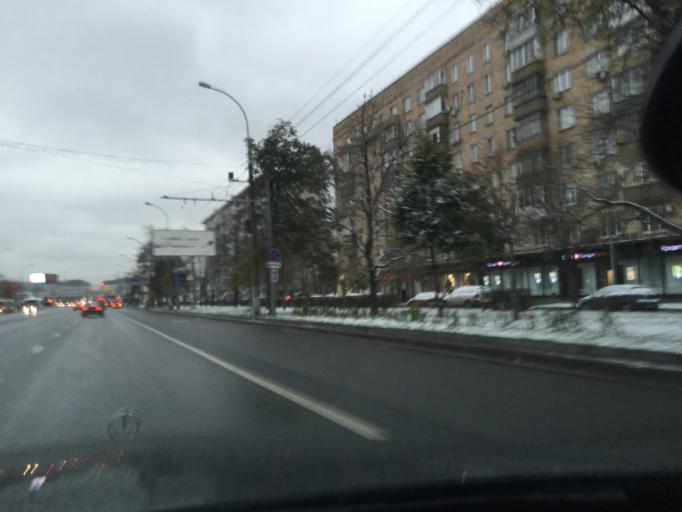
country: RU
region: Moscow
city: Luzhniki
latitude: 55.7208
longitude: 37.5733
